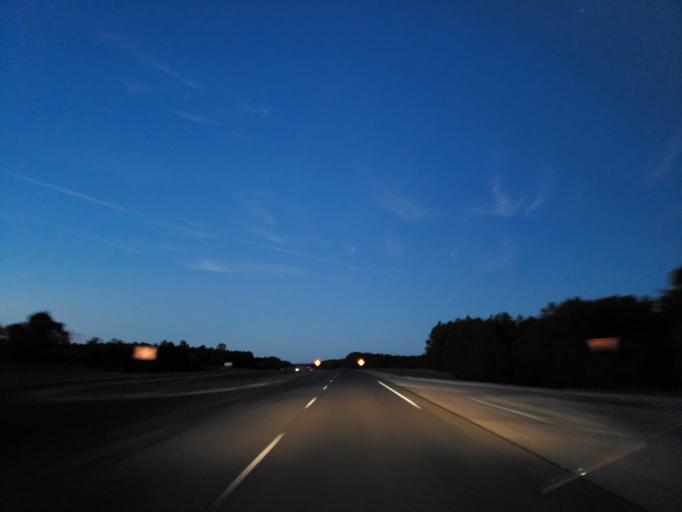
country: US
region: Mississippi
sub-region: Clarke County
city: Quitman
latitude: 32.0074
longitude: -88.6898
